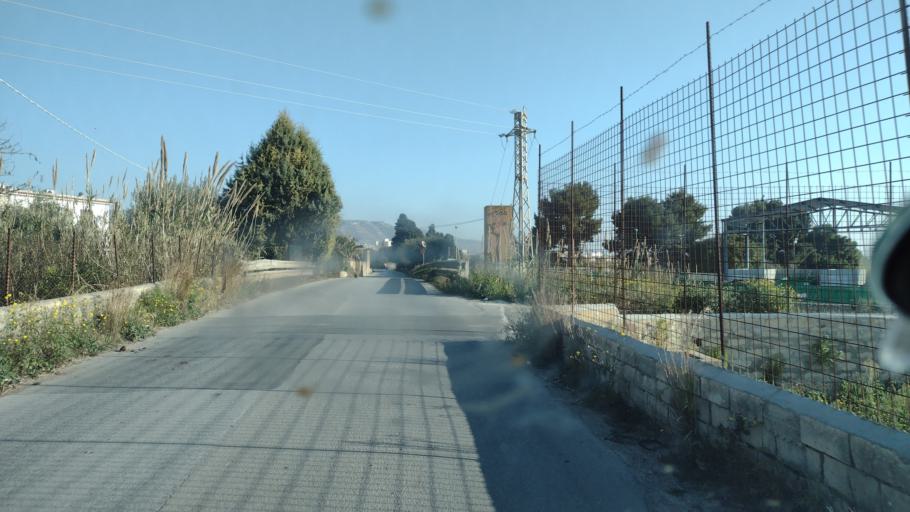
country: IT
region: Sicily
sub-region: Provincia di Siracusa
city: Avola
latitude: 36.8972
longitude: 15.1341
